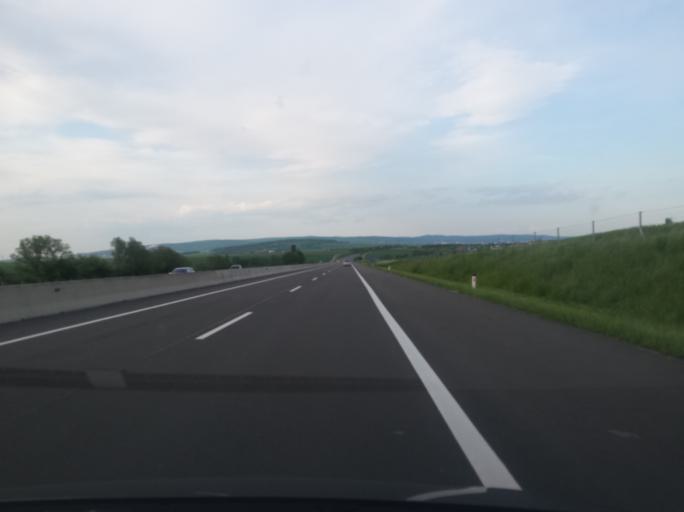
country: AT
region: Burgenland
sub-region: Politischer Bezirk Mattersburg
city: Hirm
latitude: 47.7801
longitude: 16.4361
